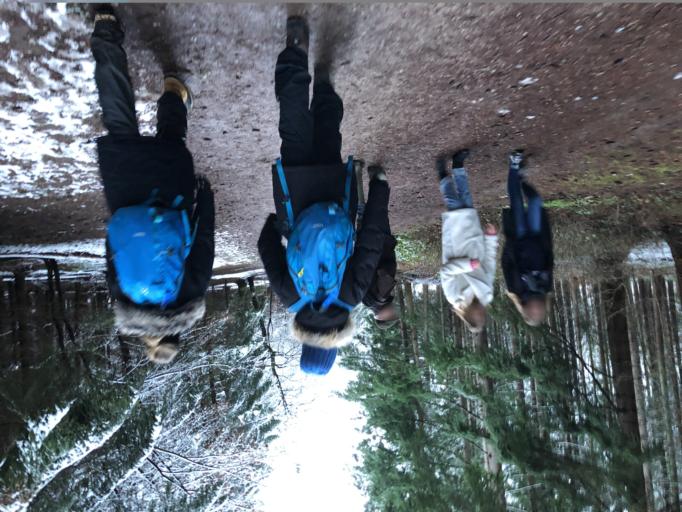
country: DK
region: Capital Region
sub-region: Rudersdal Kommune
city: Holte
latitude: 55.8081
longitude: 12.4827
